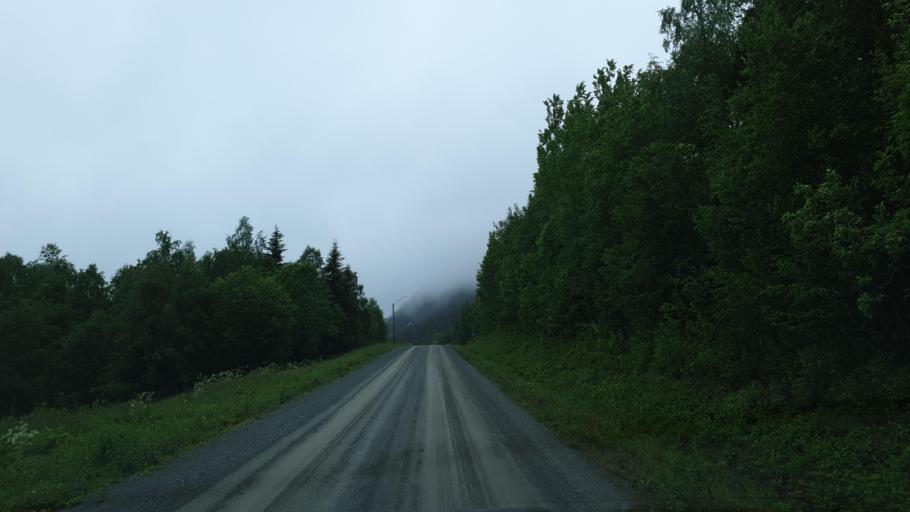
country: SE
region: Vaesterbotten
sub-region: Vilhelmina Kommun
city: Sjoberg
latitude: 65.3441
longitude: 15.8676
